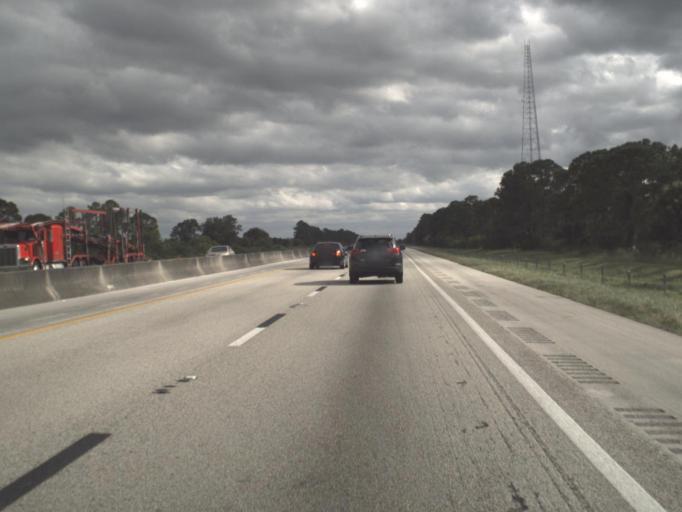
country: US
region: Florida
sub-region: Martin County
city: Port Salerno
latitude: 27.0919
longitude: -80.2559
